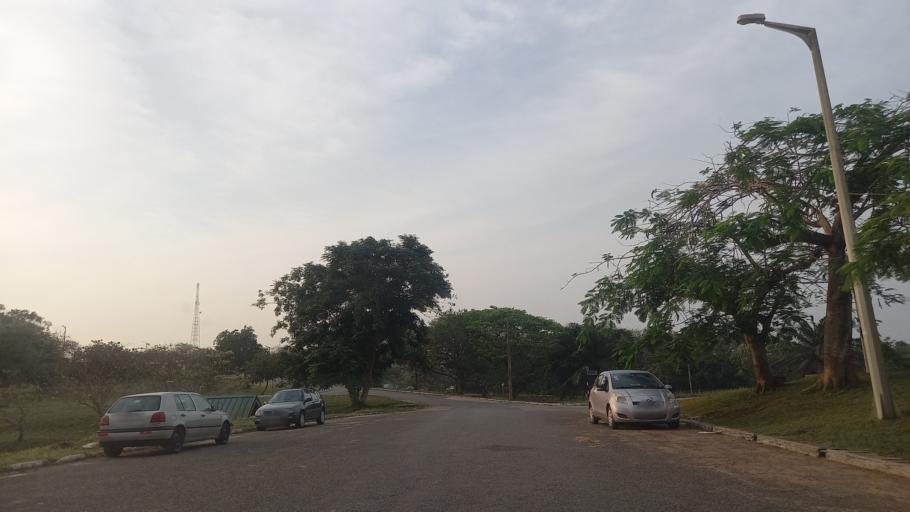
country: GH
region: Western
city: Shama Junction
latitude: 4.9818
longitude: -1.6599
